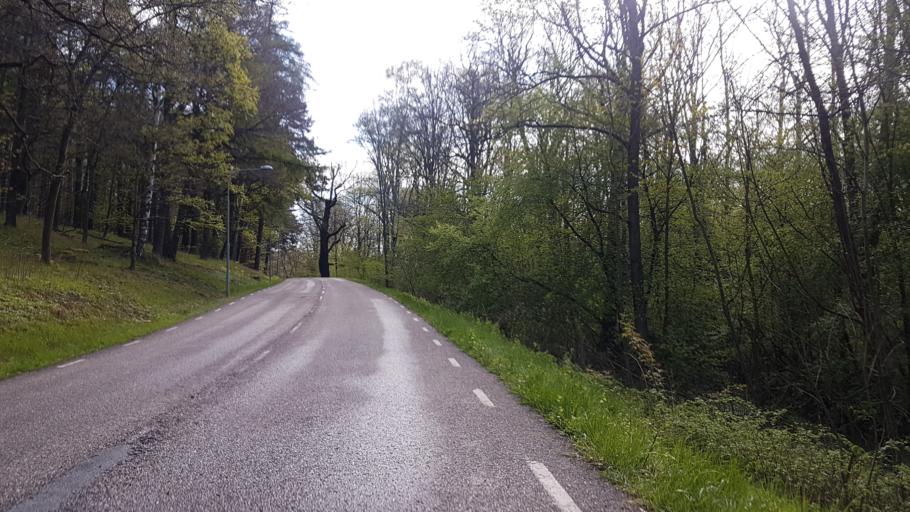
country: SE
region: Stockholm
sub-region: Stockholms Kommun
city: OEstermalm
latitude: 59.3557
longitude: 18.0718
